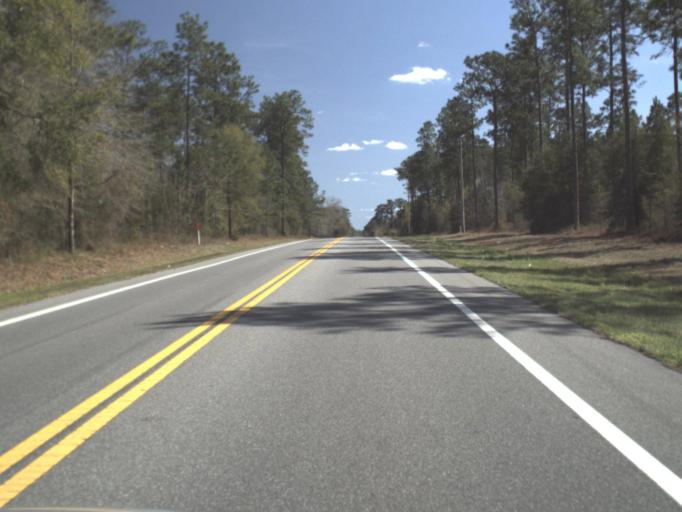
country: US
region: Florida
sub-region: Gadsden County
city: Gretna
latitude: 30.6702
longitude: -84.7008
